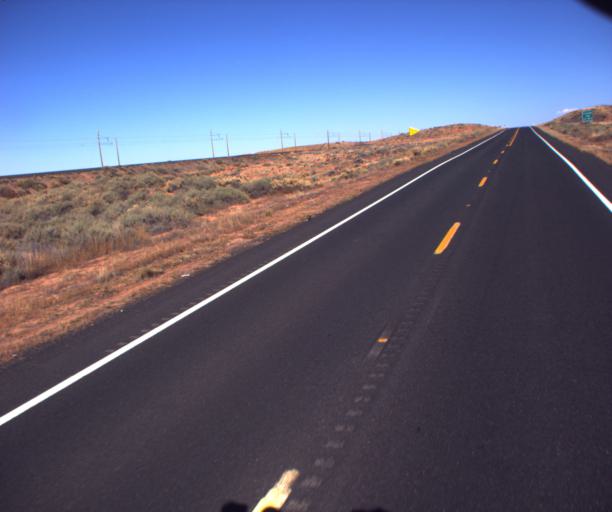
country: US
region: Arizona
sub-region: Coconino County
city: Kaibito
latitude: 36.3942
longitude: -110.8727
